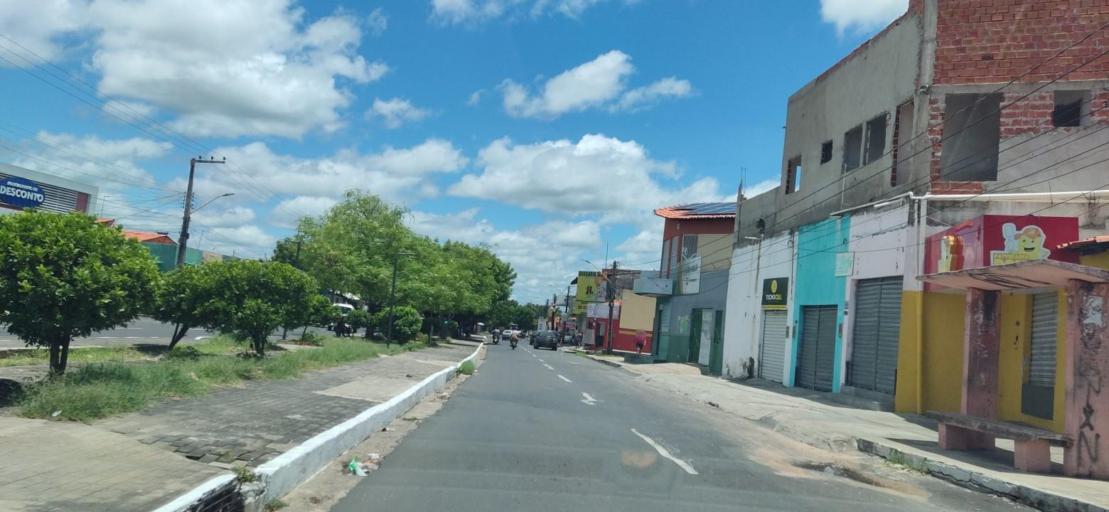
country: BR
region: Piaui
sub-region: Teresina
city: Teresina
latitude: -5.1508
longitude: -42.7857
